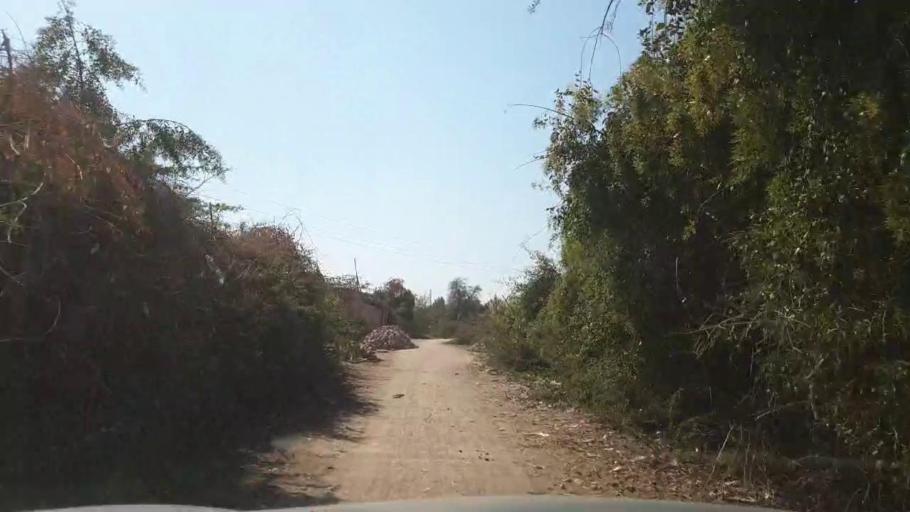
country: PK
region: Sindh
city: Tando Adam
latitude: 25.6357
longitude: 68.7054
